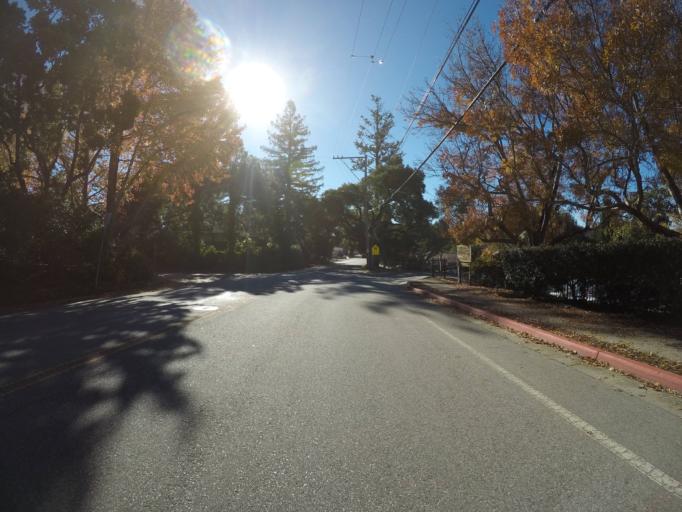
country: US
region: California
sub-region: Santa Cruz County
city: Scotts Valley
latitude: 37.0479
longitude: -122.0242
